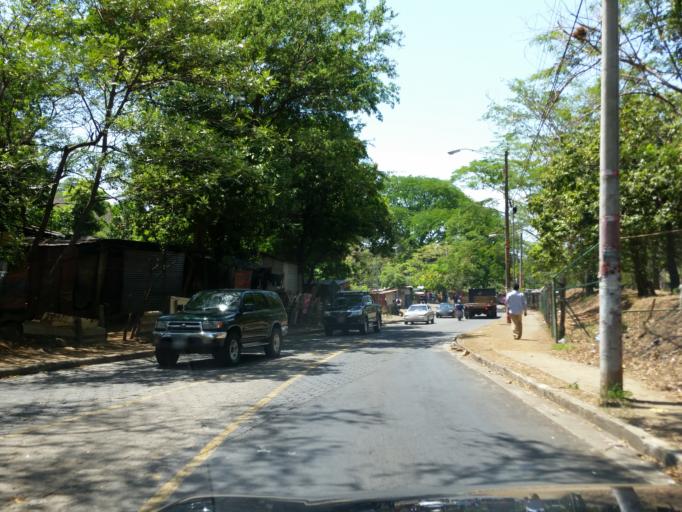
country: NI
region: Managua
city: Managua
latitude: 12.1043
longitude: -86.2724
